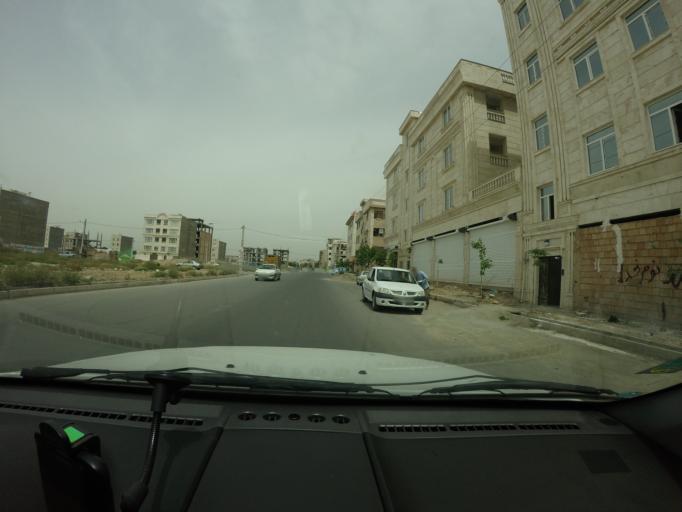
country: IR
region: Tehran
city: Eslamshahr
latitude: 35.5311
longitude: 51.2122
